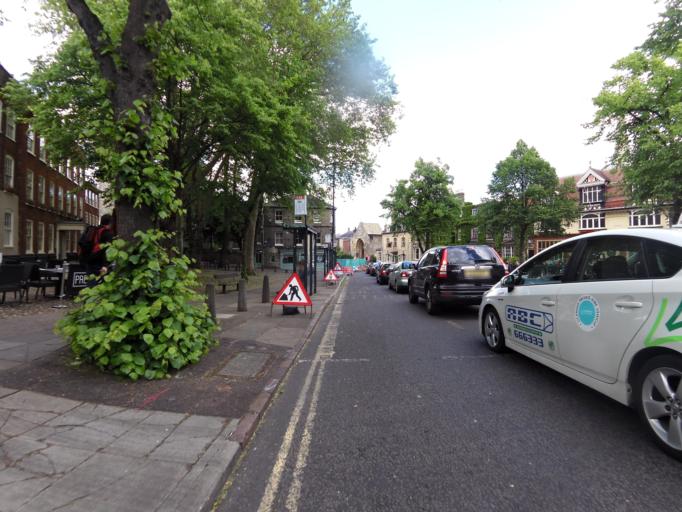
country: GB
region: England
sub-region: Norfolk
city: Norwich
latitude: 52.6307
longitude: 1.2987
